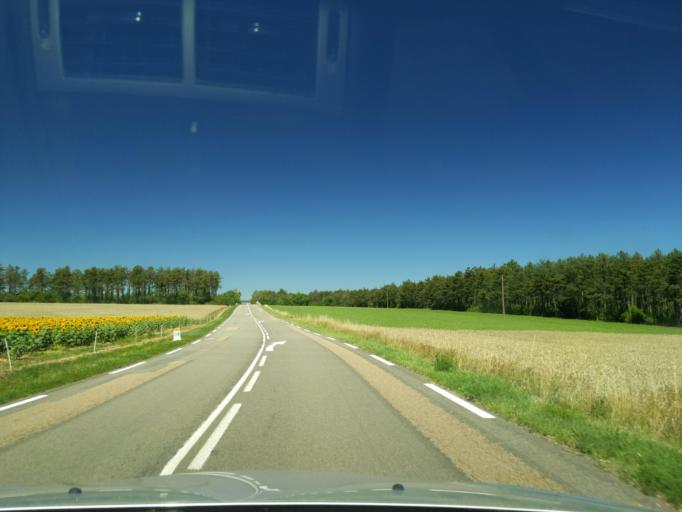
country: FR
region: Bourgogne
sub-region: Departement de la Cote-d'Or
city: Is-sur-Tille
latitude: 47.5015
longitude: 5.0833
